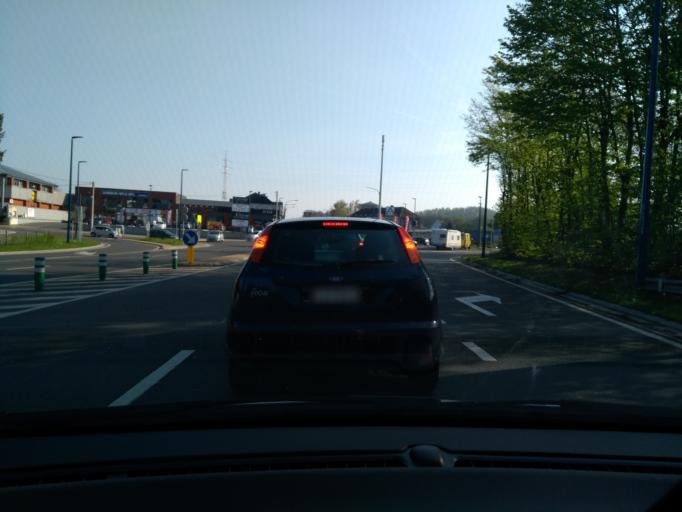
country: BE
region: Wallonia
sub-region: Province du Hainaut
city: Chapelle-lez-Herlaimont
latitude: 50.4687
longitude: 4.2686
